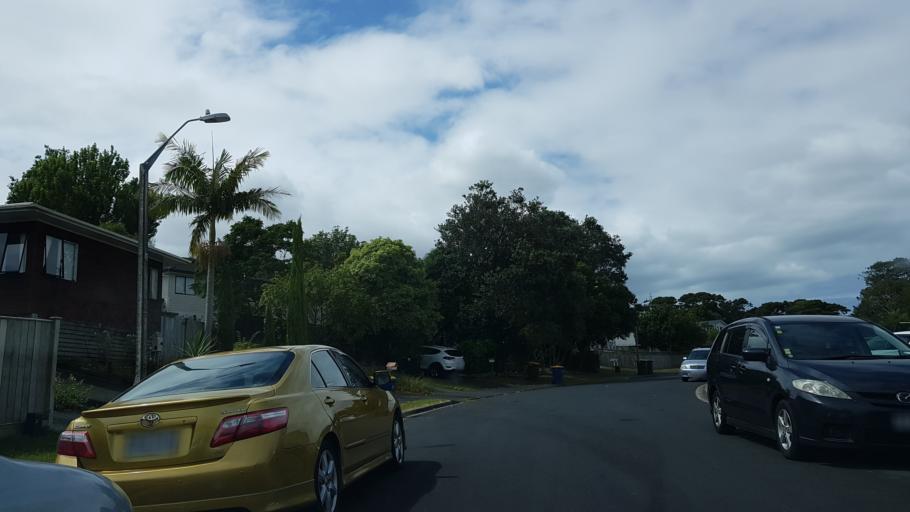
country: NZ
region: Auckland
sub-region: Auckland
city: North Shore
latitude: -36.7812
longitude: 174.7077
